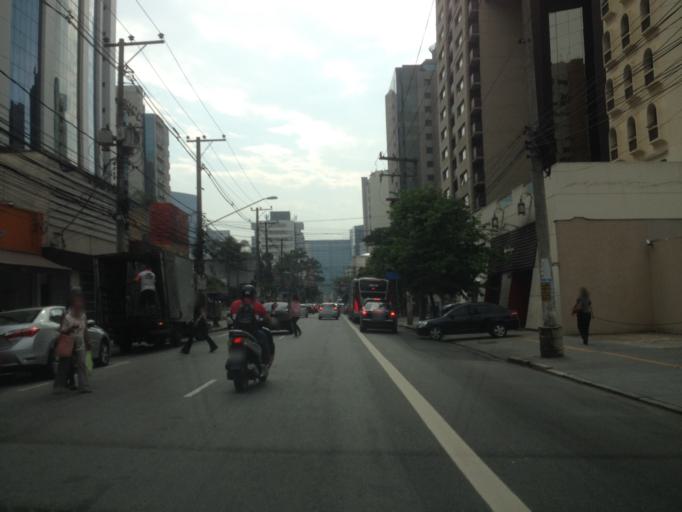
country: BR
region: Sao Paulo
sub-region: Sao Paulo
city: Sao Paulo
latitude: -23.5845
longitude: -46.6743
